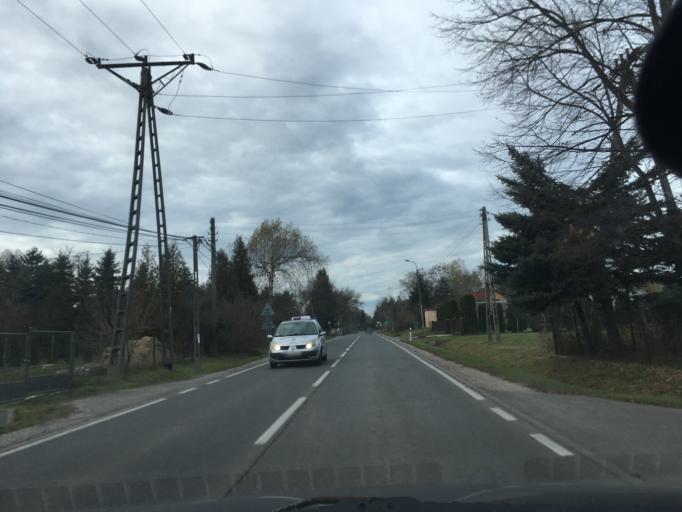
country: PL
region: Masovian Voivodeship
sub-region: Powiat piaseczynski
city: Tarczyn
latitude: 51.9787
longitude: 20.8905
